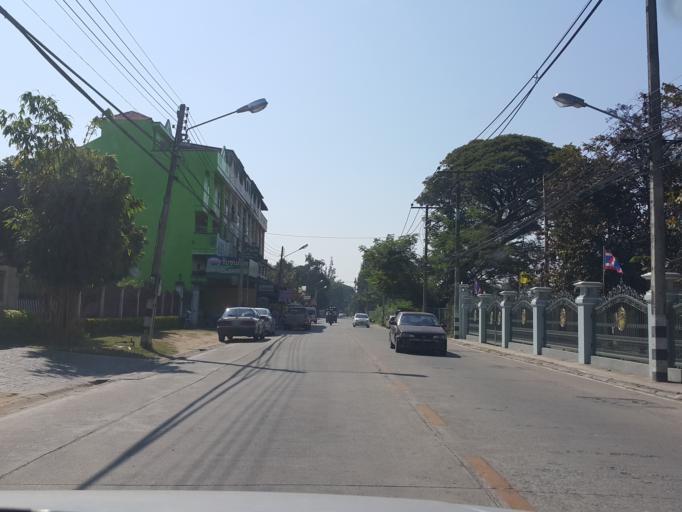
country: TH
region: Chiang Mai
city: Chiang Mai
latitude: 18.7891
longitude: 99.0179
